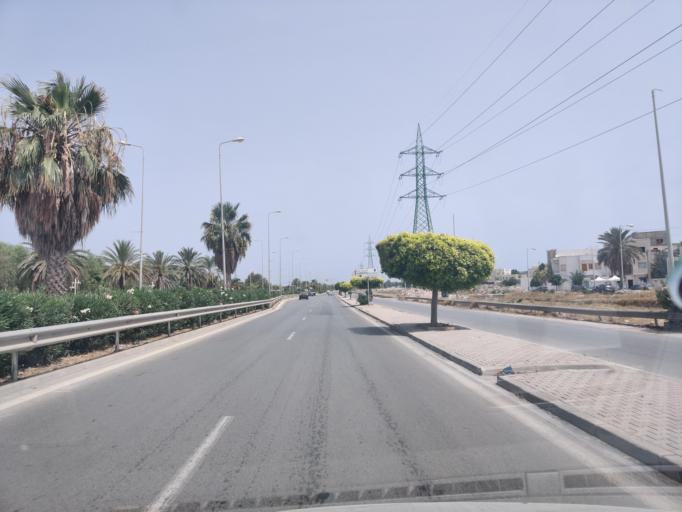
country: TN
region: Tunis
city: Carthage
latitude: 36.8497
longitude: 10.3050
